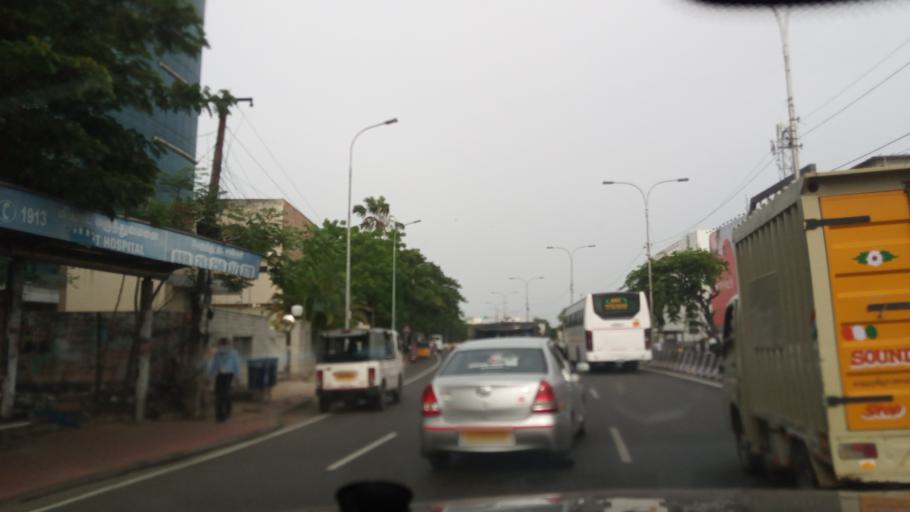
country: IN
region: Tamil Nadu
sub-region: Kancheepuram
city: Manappakkam
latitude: 13.0210
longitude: 80.1839
